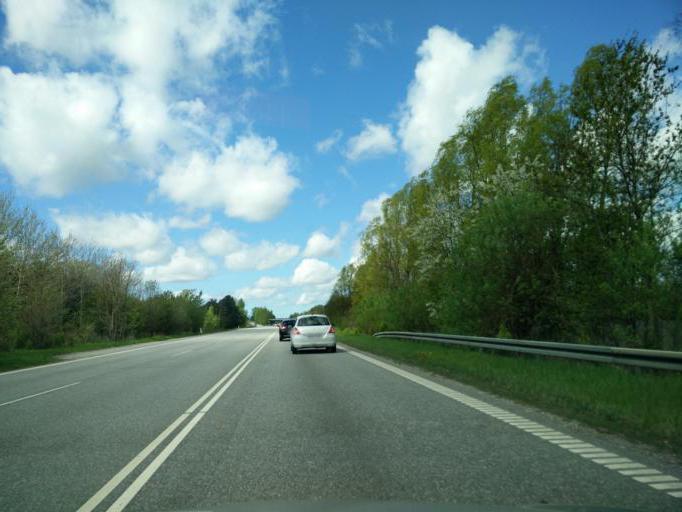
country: DK
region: Capital Region
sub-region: Allerod Kommune
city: Lillerod
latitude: 55.8588
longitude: 12.3210
